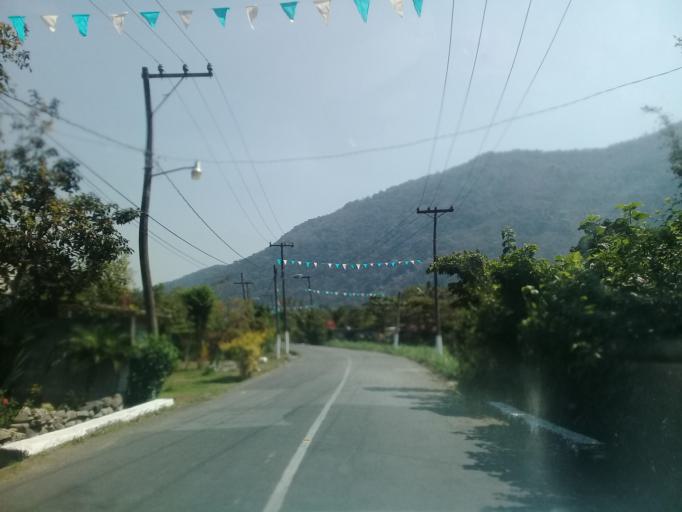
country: MX
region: Veracruz
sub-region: Ixtaczoquitlan
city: Capoluca
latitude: 18.8035
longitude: -96.9926
